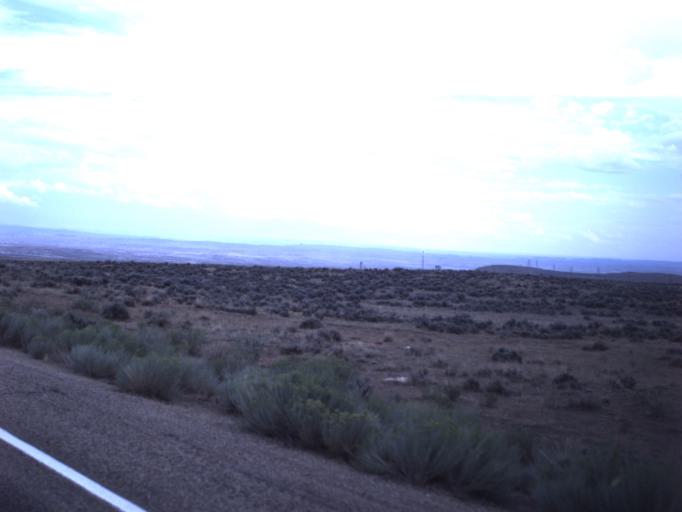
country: US
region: Utah
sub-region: Uintah County
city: Naples
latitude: 40.1521
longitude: -109.3016
